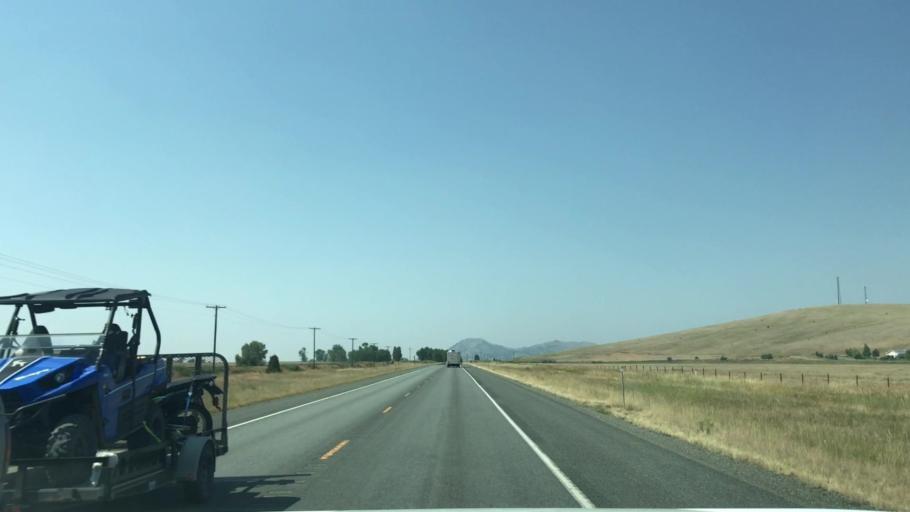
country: US
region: Montana
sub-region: Broadwater County
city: Townsend
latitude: 46.4625
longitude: -111.6444
